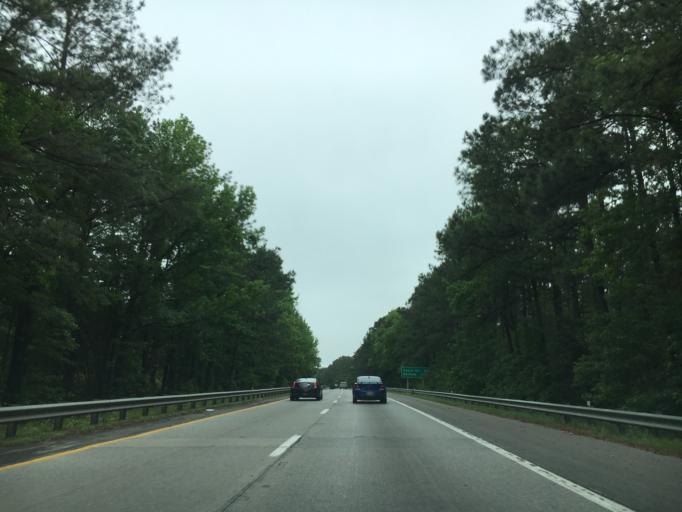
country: US
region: Virginia
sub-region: Chesterfield County
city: Matoaca
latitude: 37.1970
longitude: -77.4783
